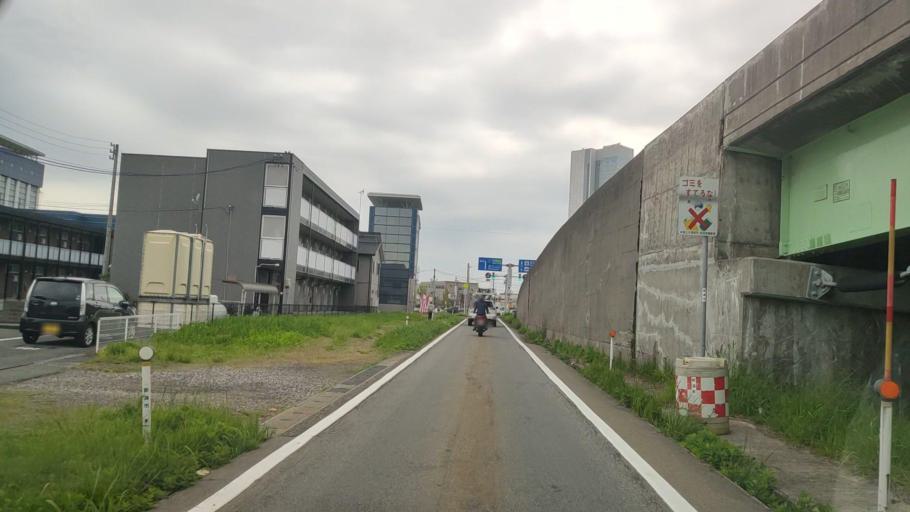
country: JP
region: Niigata
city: Niigata-shi
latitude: 37.9261
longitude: 139.0664
